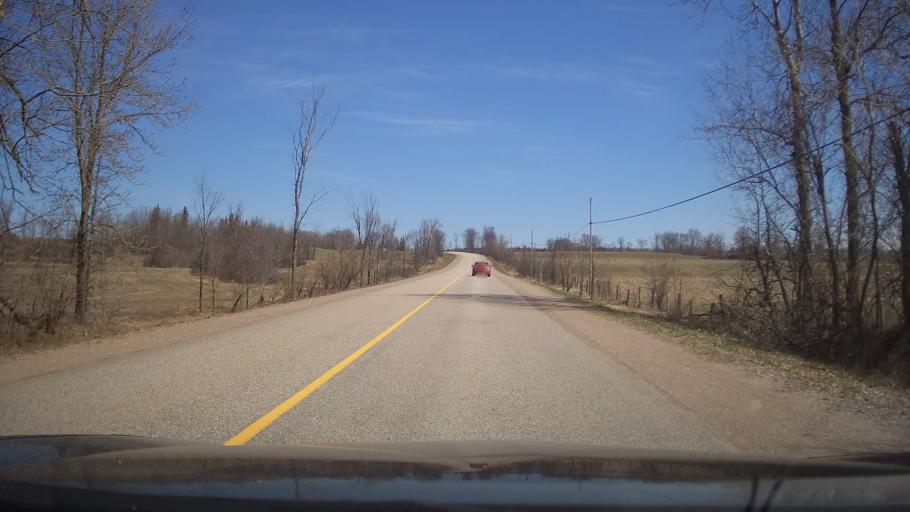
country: CA
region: Ontario
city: Arnprior
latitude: 45.5321
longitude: -76.3722
